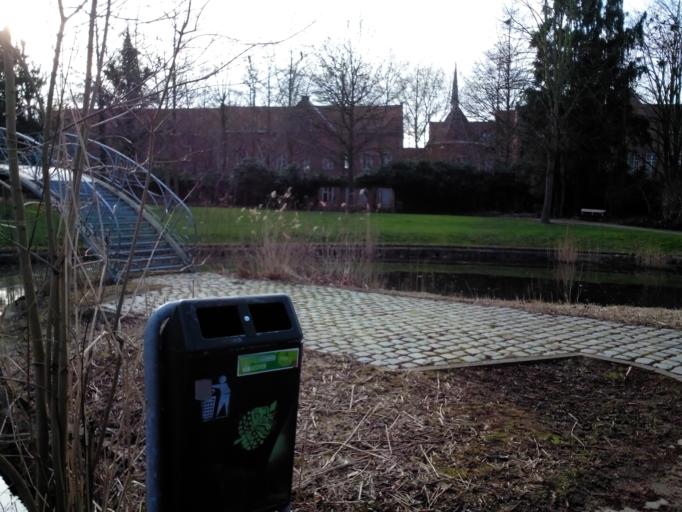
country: BE
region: Flanders
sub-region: Provincie Vlaams-Brabant
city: Leuven
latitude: 50.8739
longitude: 4.6971
